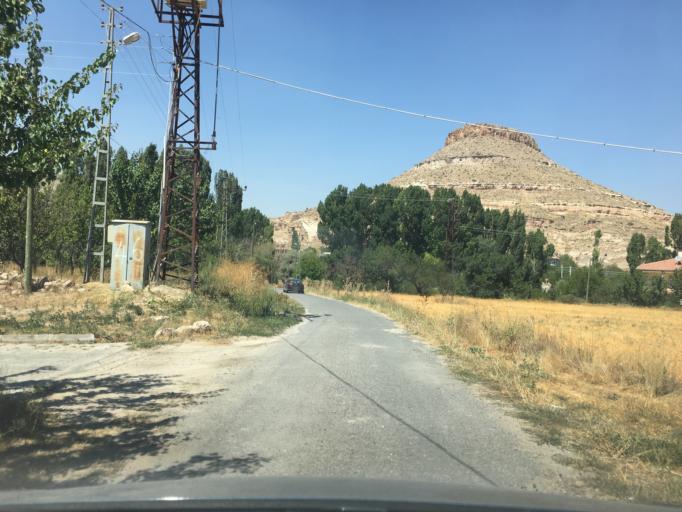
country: TR
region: Nevsehir
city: Urgub
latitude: 38.4689
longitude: 34.9612
